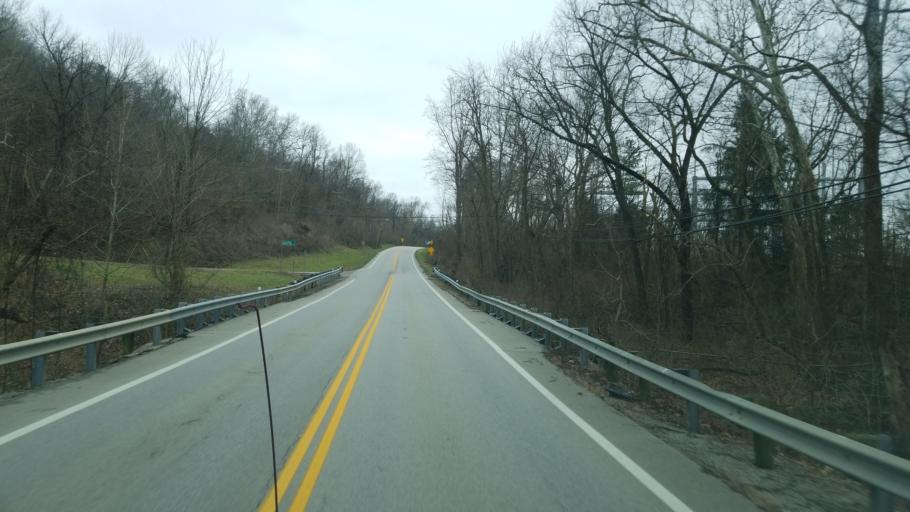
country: US
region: Ohio
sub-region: Clermont County
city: New Richmond
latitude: 38.8675
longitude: -84.2241
